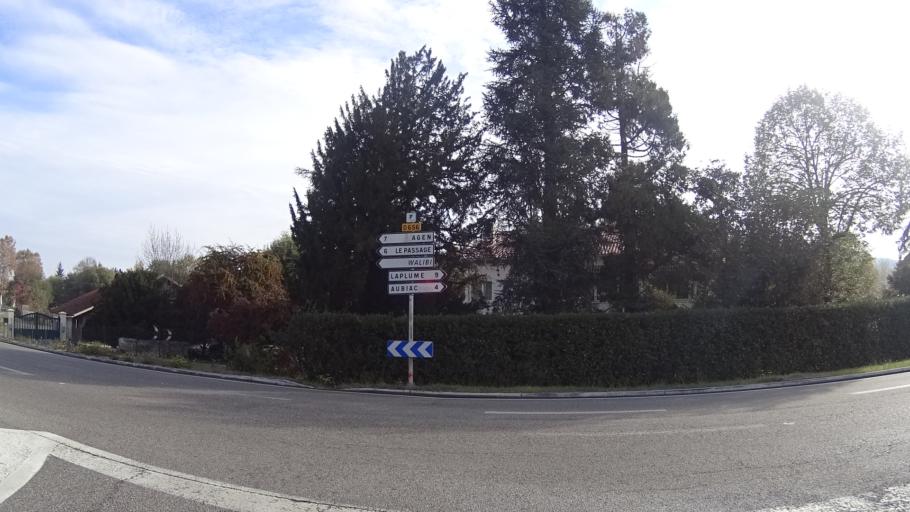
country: FR
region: Aquitaine
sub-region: Departement du Lot-et-Garonne
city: Roquefort
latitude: 44.1711
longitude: 0.5520
